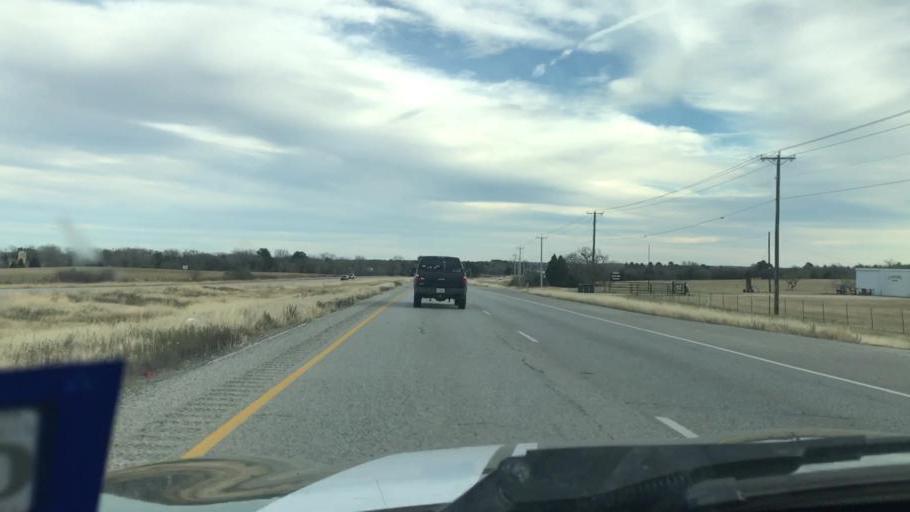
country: US
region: Texas
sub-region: Bastrop County
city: Elgin
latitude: 30.3218
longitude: -97.3207
